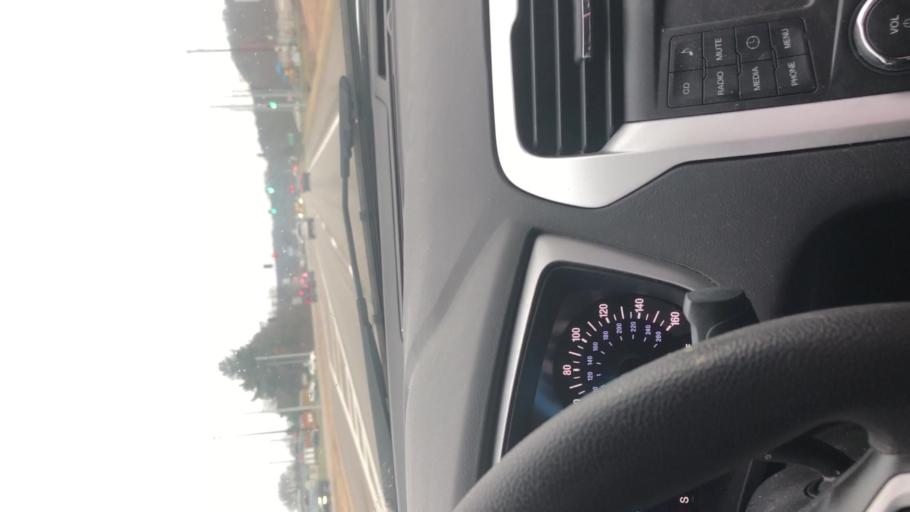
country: US
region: Ohio
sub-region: Lawrence County
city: South Point
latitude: 38.4453
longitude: -82.5875
